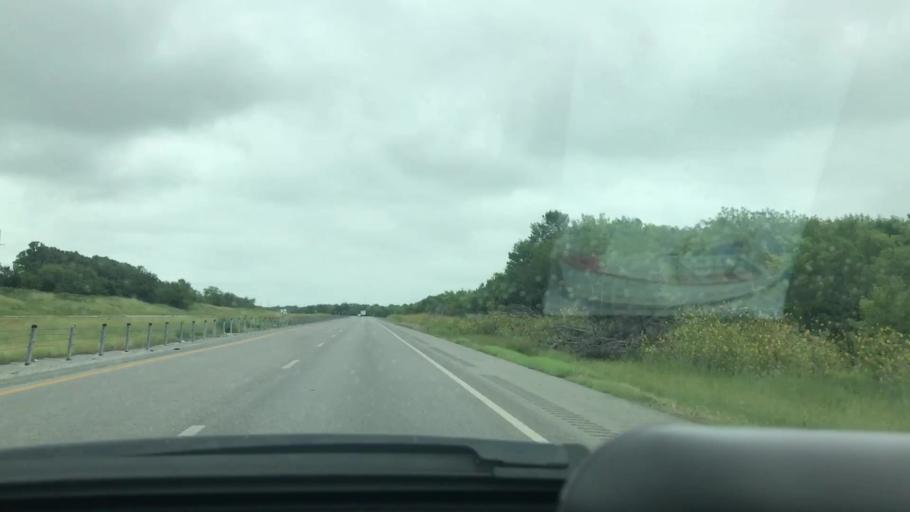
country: US
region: Oklahoma
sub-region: Coal County
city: Coalgate
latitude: 34.6437
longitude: -95.9482
